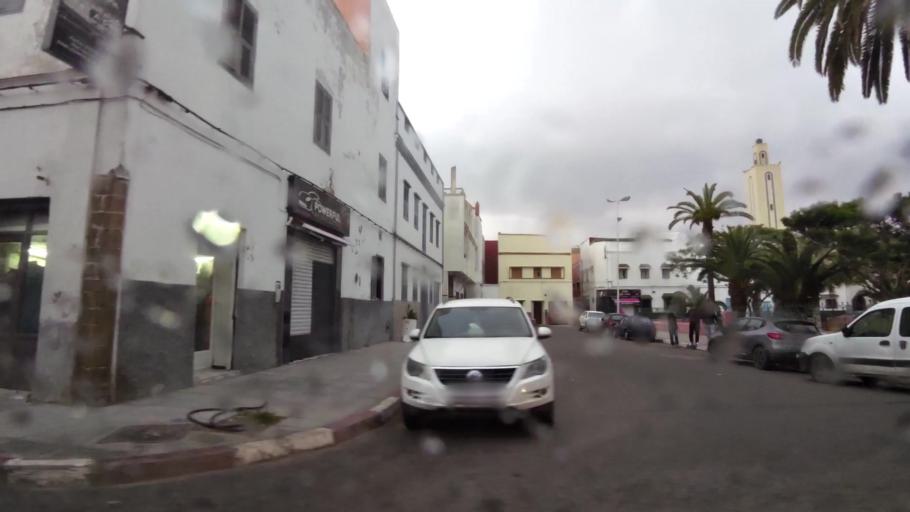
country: MA
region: Doukkala-Abda
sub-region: El-Jadida
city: El Jadida
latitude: 33.2586
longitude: -8.5059
